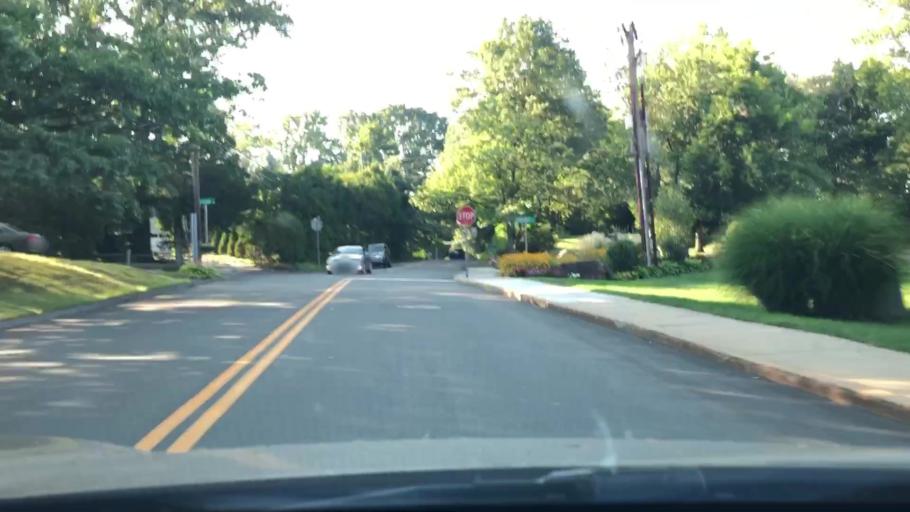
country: US
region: Connecticut
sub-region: Fairfield County
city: Norwalk
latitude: 41.1060
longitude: -73.4429
